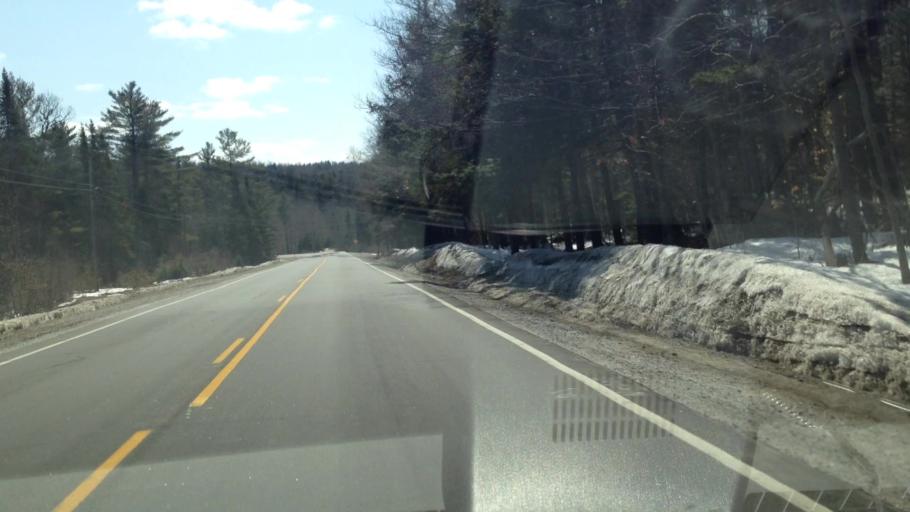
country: US
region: New Hampshire
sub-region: Merrimack County
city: Wilmot
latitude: 43.4673
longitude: -71.9601
